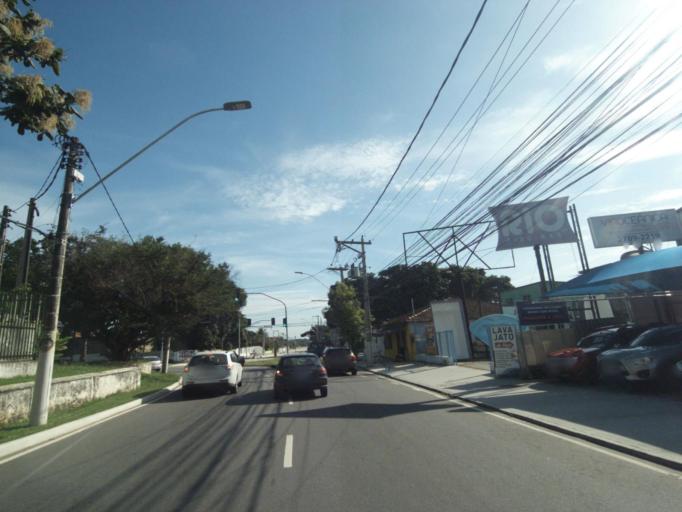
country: BR
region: Rio de Janeiro
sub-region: Niteroi
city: Niteroi
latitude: -22.9319
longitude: -43.0671
